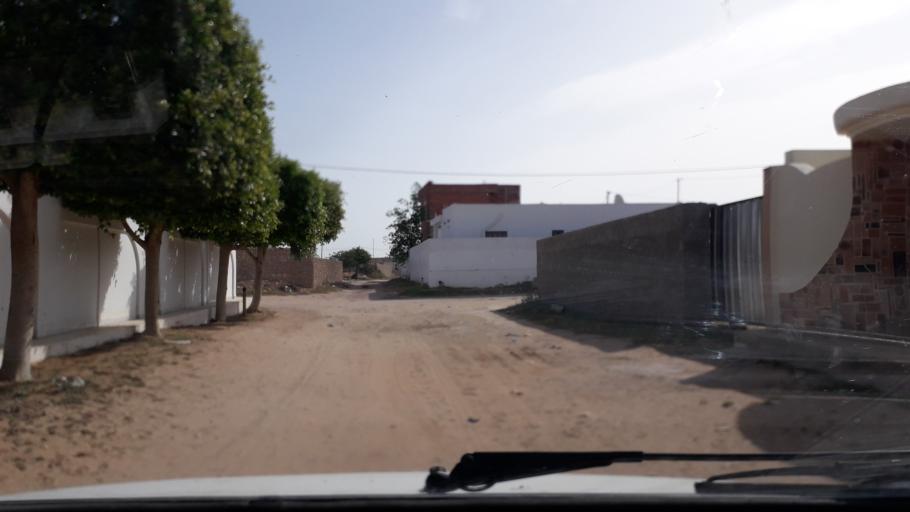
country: TN
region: Safaqis
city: Al Qarmadah
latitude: 34.8080
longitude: 10.7705
